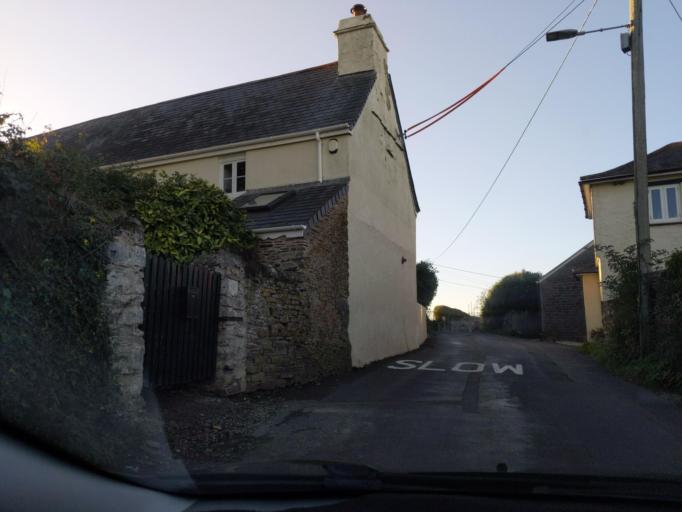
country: GB
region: England
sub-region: Plymouth
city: Plymstock
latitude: 50.3432
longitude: -4.0930
